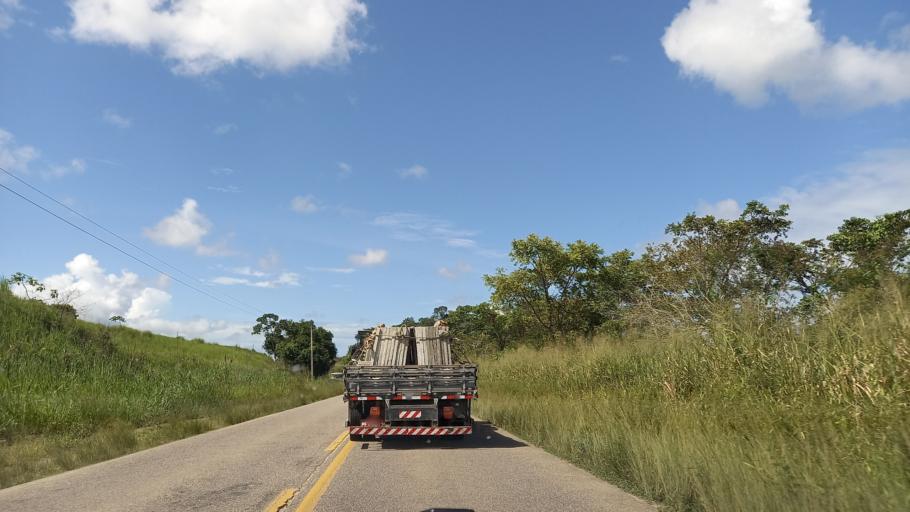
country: BR
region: Pernambuco
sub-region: Barreiros
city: Barreiros
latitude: -8.7826
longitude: -35.1776
